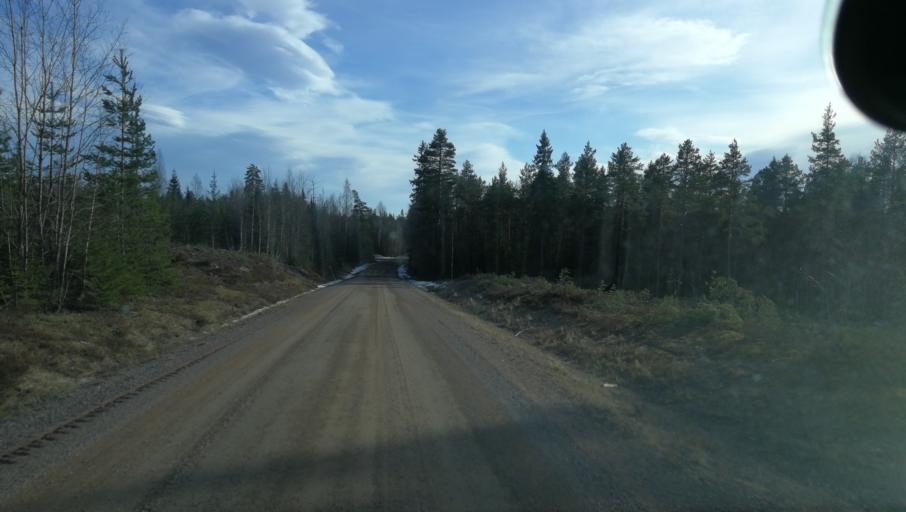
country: SE
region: Dalarna
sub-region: Vansbro Kommun
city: Vansbro
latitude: 60.8245
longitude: 14.1943
